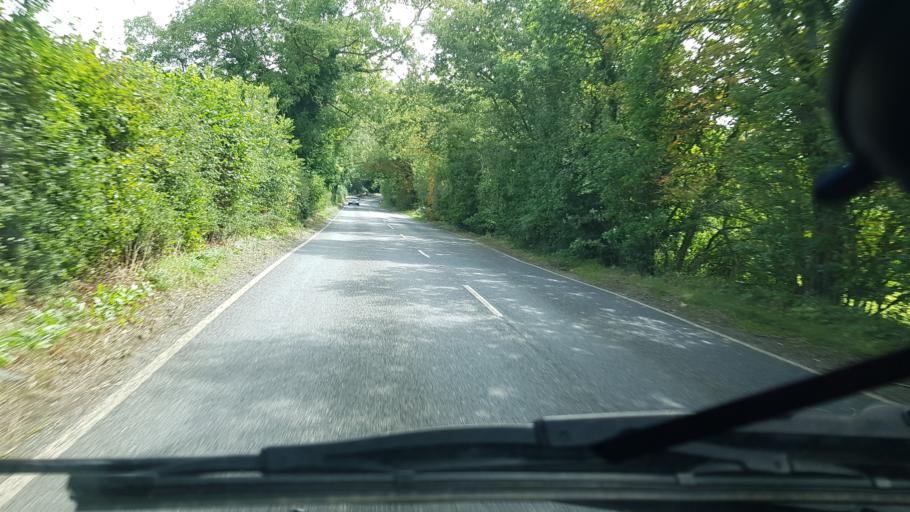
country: GB
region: England
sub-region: West Sussex
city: Rudgwick
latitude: 51.0957
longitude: -0.4807
